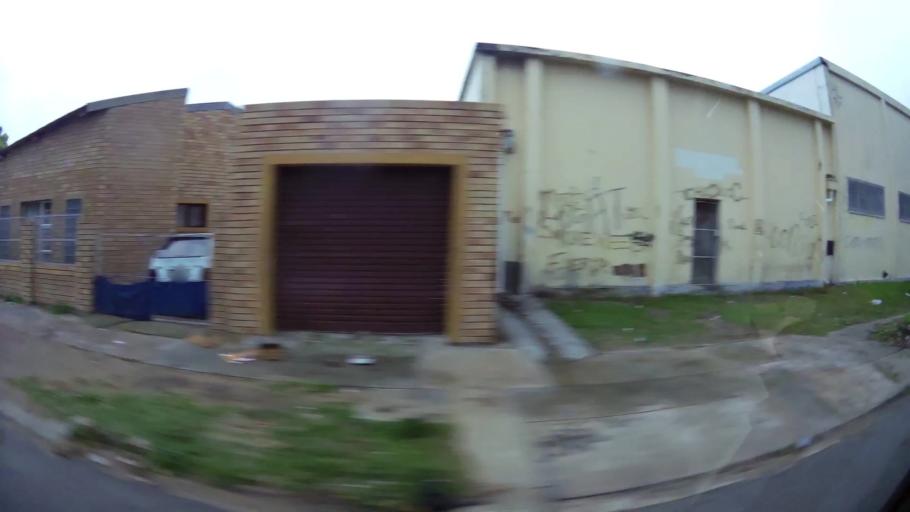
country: ZA
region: Eastern Cape
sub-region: Nelson Mandela Bay Metropolitan Municipality
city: Port Elizabeth
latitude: -33.9413
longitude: 25.5949
